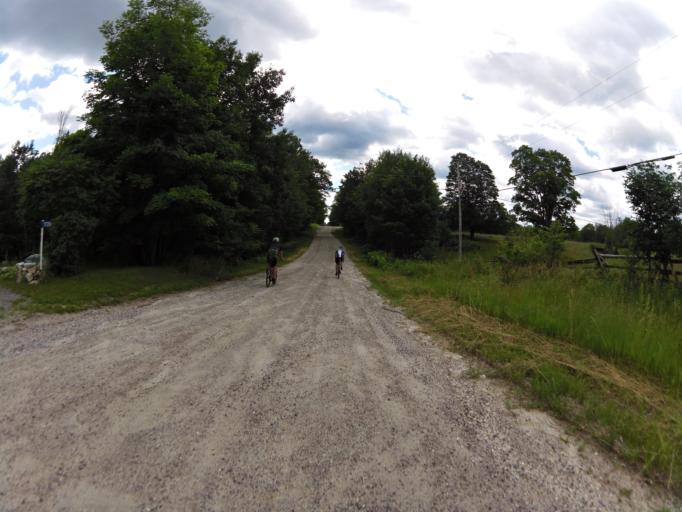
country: CA
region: Ontario
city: Perth
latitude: 45.0503
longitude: -76.4775
